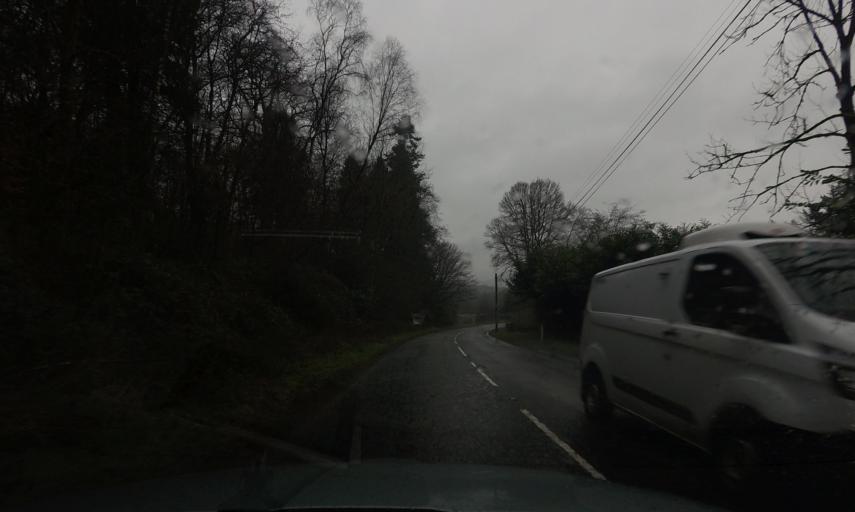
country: GB
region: Scotland
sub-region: Stirling
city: Balfron
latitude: 56.1554
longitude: -4.3637
